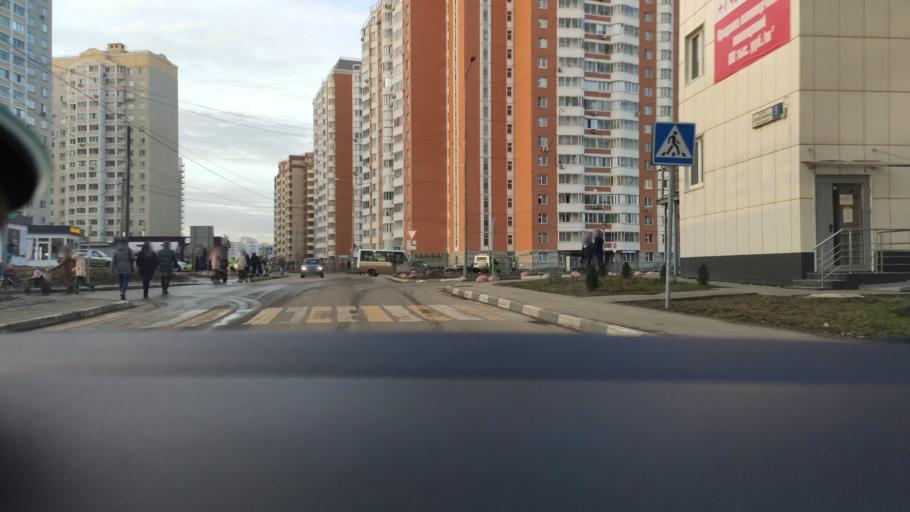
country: RU
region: Moskovskaya
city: Vidnoye
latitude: 55.5373
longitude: 37.7232
